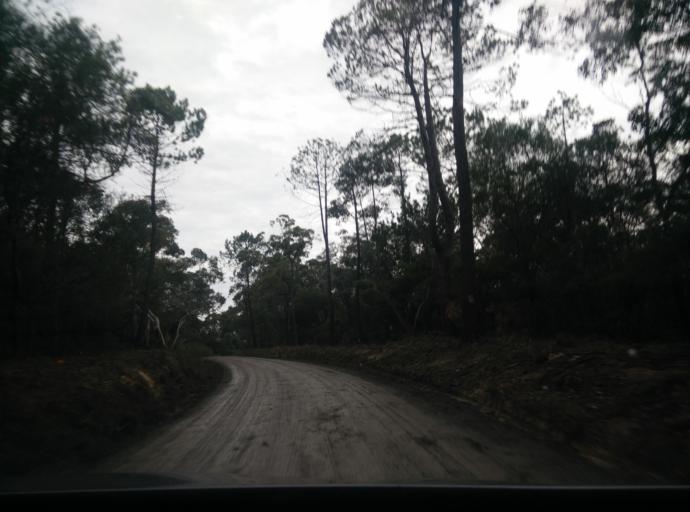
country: AU
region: New South Wales
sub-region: Gosford Shire
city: Narara
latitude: -33.3688
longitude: 151.3261
